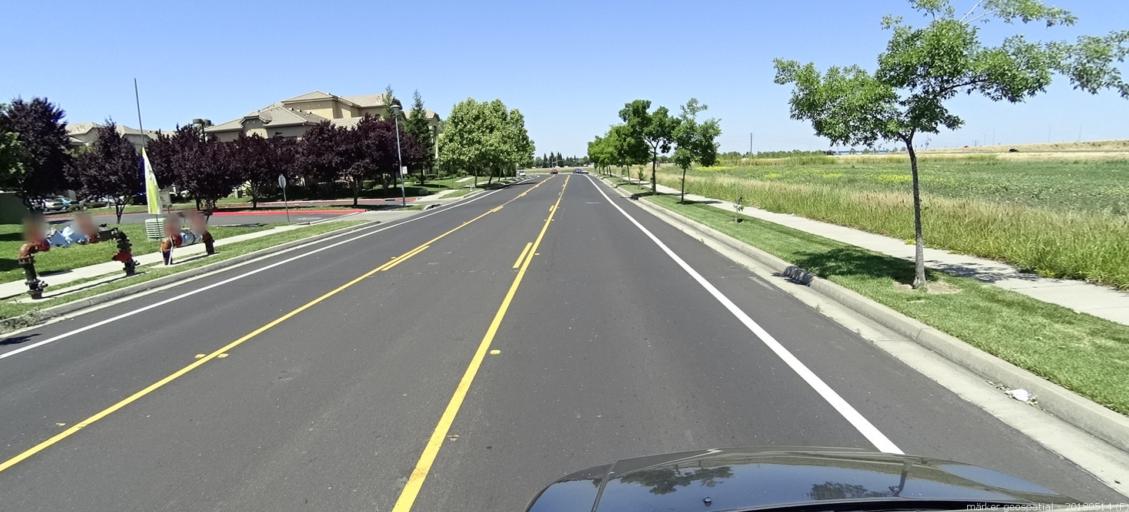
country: US
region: California
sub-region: Yolo County
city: West Sacramento
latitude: 38.6396
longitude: -121.5274
